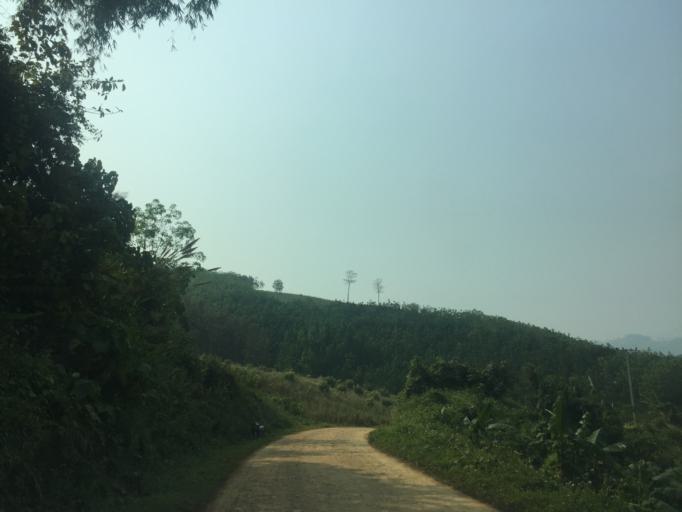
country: TH
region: Phayao
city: Phu Sang
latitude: 19.6467
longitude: 100.5255
